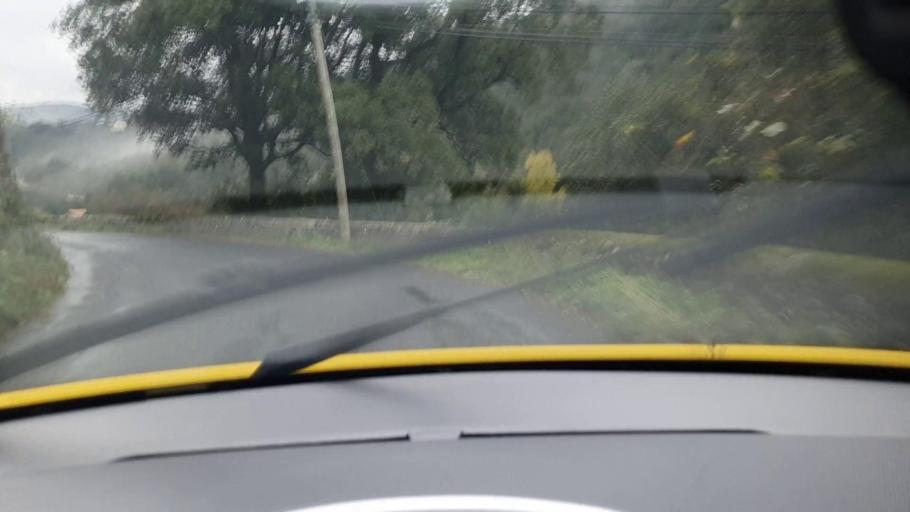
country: FR
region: Languedoc-Roussillon
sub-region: Departement du Gard
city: Sumene
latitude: 43.9954
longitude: 3.7127
